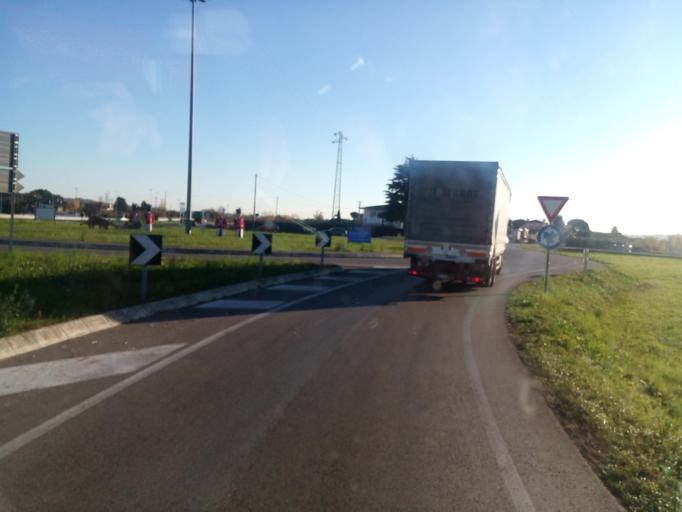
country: IT
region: Veneto
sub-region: Provincia di Vicenza
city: Thiene
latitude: 45.6939
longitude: 11.4954
